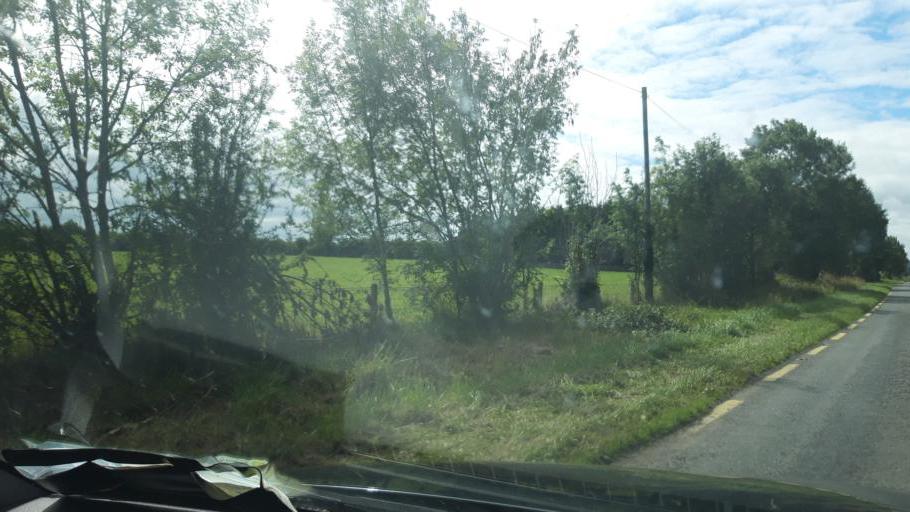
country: IE
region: Leinster
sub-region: Kilkenny
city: Callan
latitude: 52.5223
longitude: -7.4187
